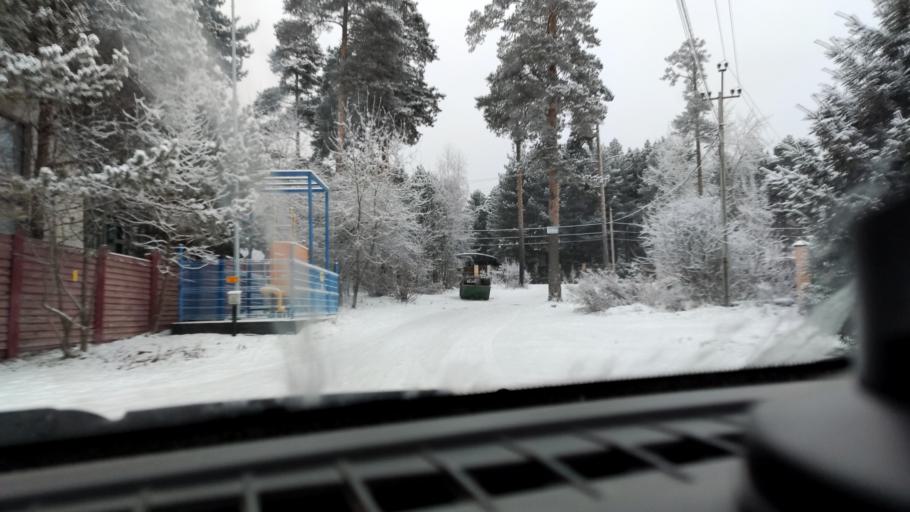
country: RU
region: Perm
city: Perm
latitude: 58.0463
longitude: 56.2821
